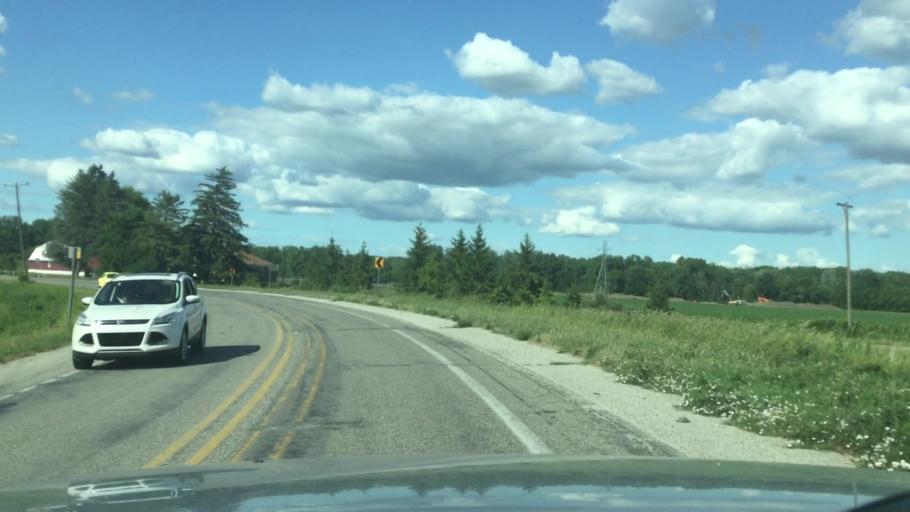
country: US
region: Michigan
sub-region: Saginaw County
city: Shields
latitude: 43.3801
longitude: -84.0153
